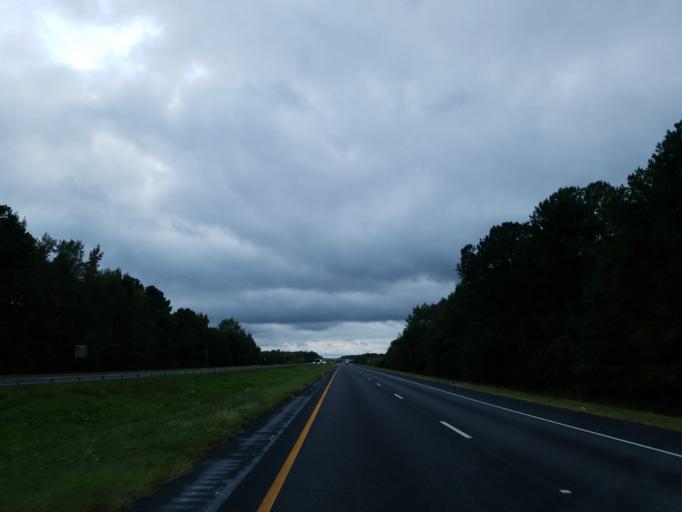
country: US
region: Alabama
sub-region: Sumter County
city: Livingston
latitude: 32.7201
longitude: -88.1206
